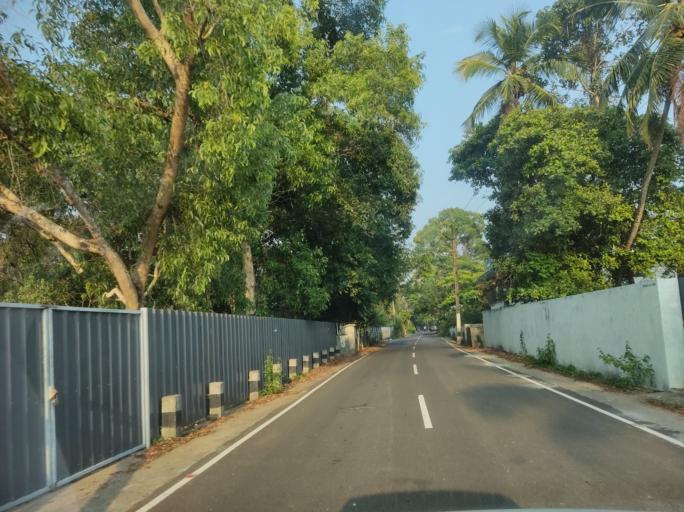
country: IN
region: Kerala
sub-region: Alappuzha
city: Alleppey
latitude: 9.5907
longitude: 76.3112
